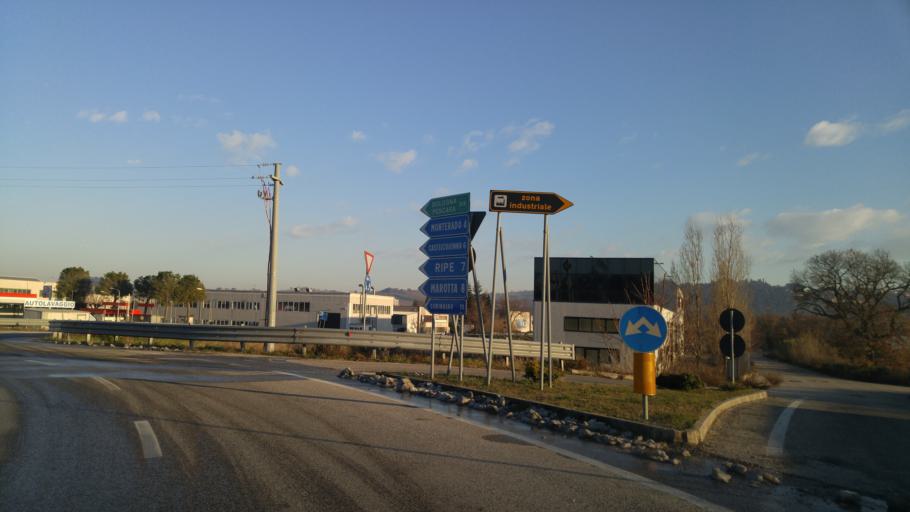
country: IT
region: The Marches
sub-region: Provincia di Ancona
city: Monterado
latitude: 43.7098
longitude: 13.0746
